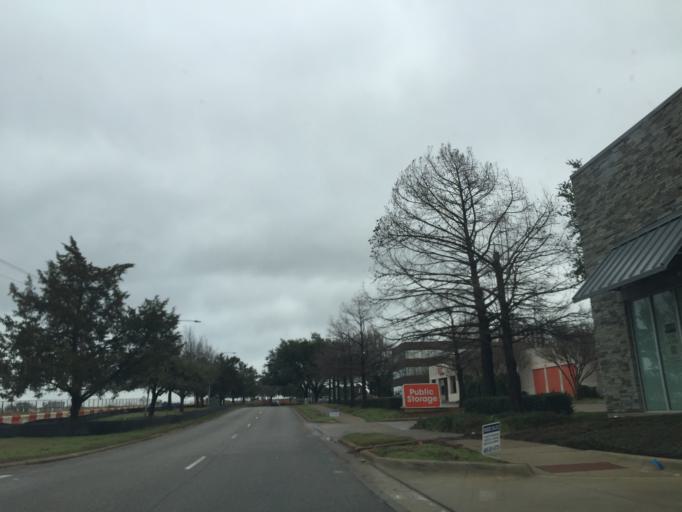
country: US
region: Texas
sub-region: Tarrant County
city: Arlington
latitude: 32.7616
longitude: -97.1085
